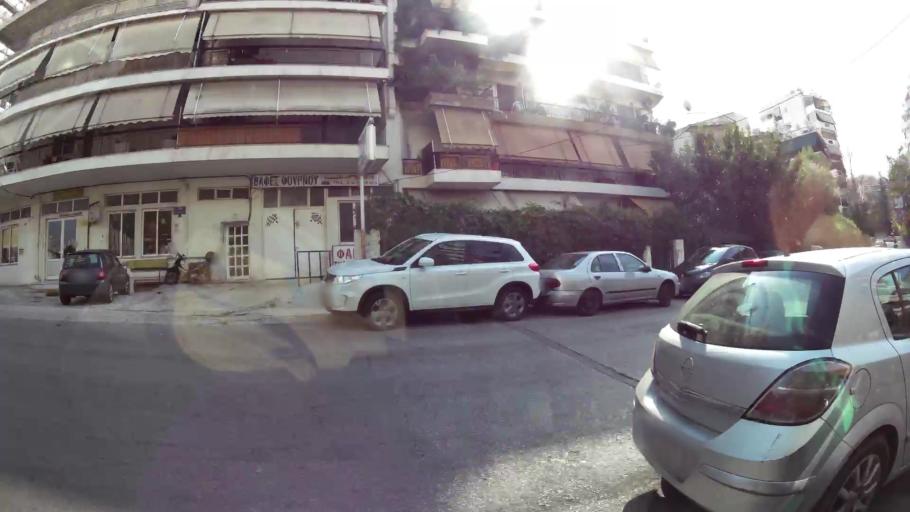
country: GR
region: Attica
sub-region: Nomarchia Athinas
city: Galatsi
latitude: 38.0133
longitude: 23.7482
